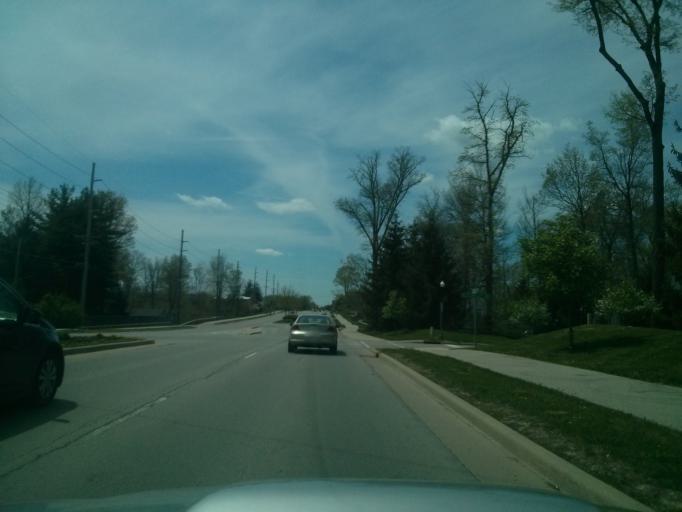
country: US
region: Indiana
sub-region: Hamilton County
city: Carmel
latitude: 39.9568
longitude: -86.1320
